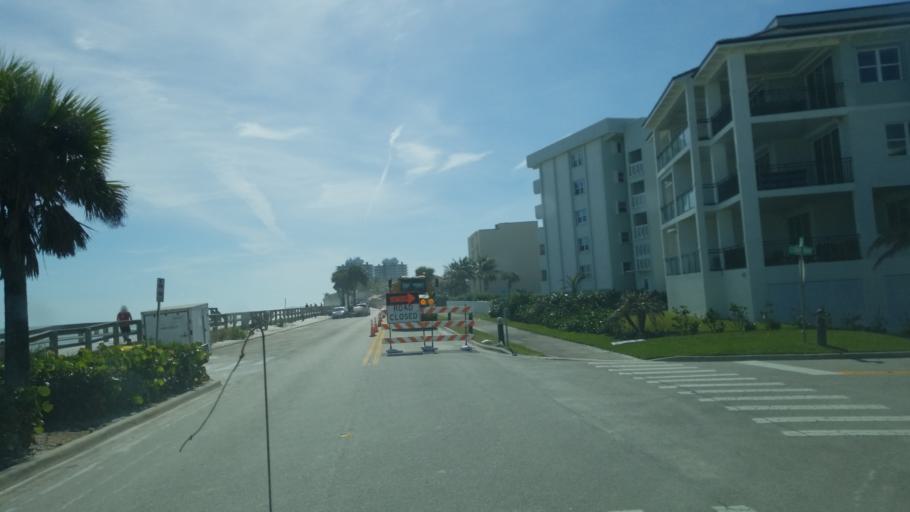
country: US
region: Florida
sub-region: Indian River County
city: Vero Beach
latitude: 27.6625
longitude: -80.3584
